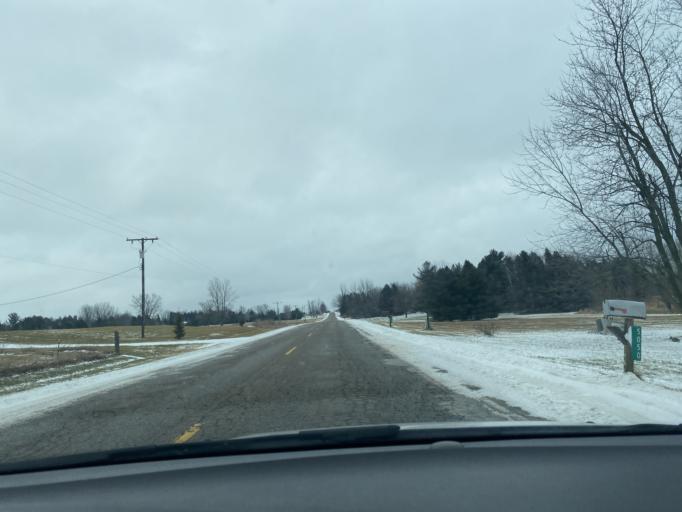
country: US
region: Michigan
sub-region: Lapeer County
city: North Branch
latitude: 43.2087
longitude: -83.1538
